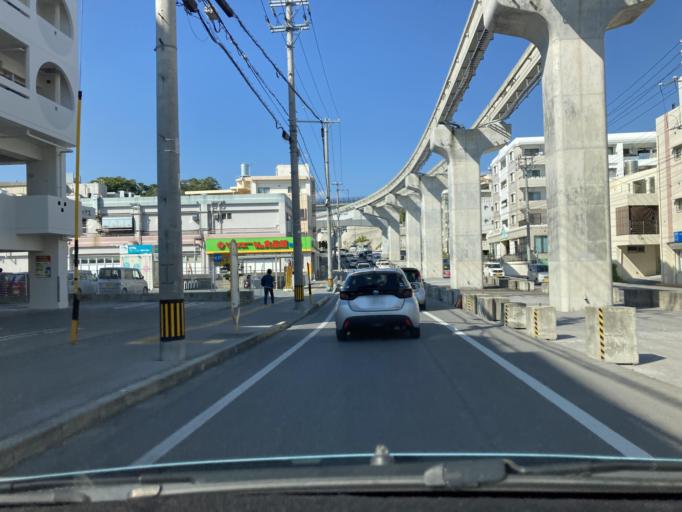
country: JP
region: Okinawa
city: Ginowan
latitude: 26.2331
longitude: 127.7287
